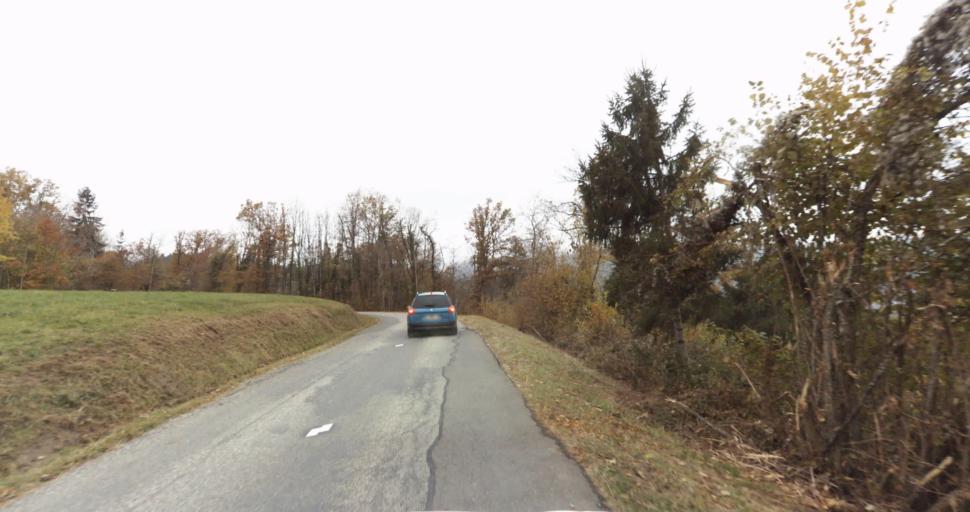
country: FR
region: Rhone-Alpes
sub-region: Departement de la Haute-Savoie
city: Saint-Jorioz
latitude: 45.8208
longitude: 6.1699
